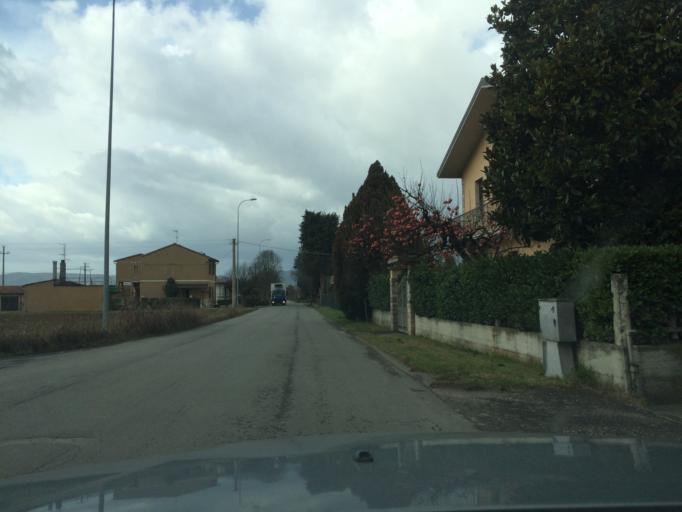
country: IT
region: Umbria
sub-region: Provincia di Terni
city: Terni
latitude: 42.5522
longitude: 12.5973
